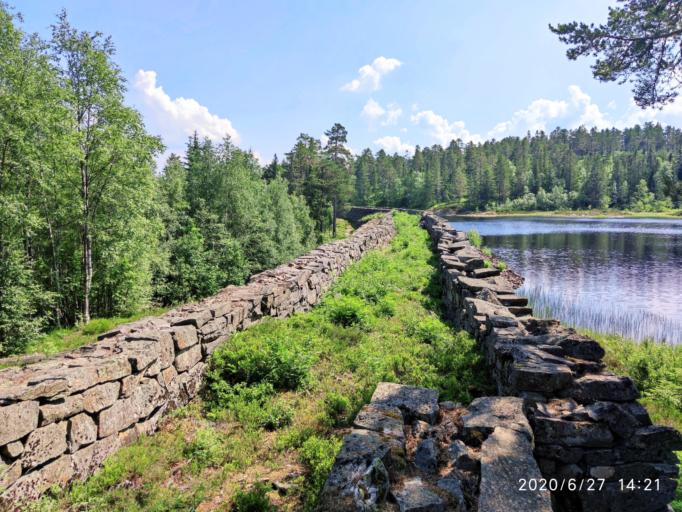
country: NO
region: Buskerud
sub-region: Kongsberg
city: Kongsberg
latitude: 59.6648
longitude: 9.5923
